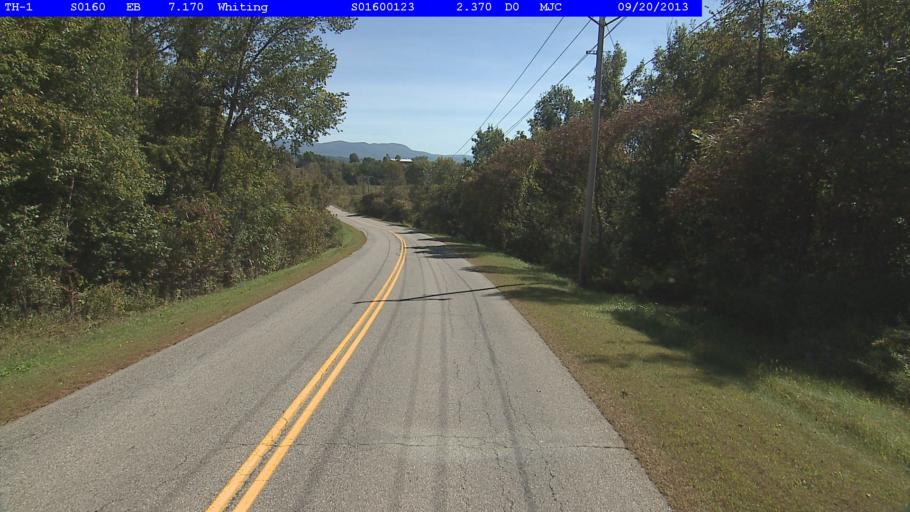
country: US
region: Vermont
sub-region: Rutland County
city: Brandon
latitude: 43.8553
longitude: -73.1827
